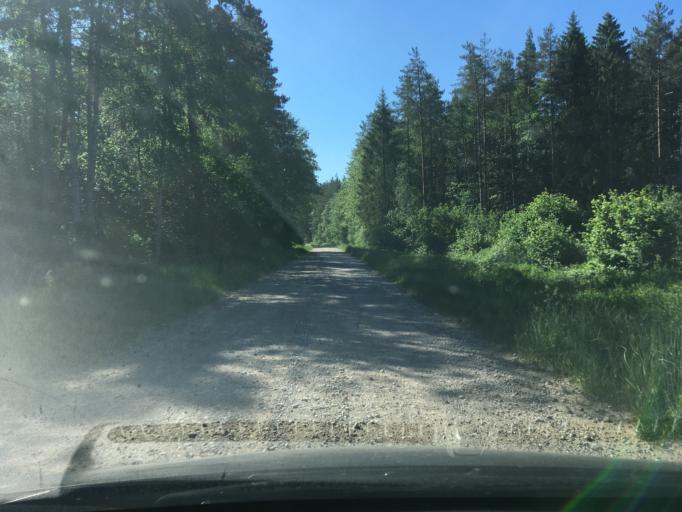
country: EE
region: Laeaene
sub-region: Lihula vald
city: Lihula
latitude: 58.6404
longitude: 23.7903
